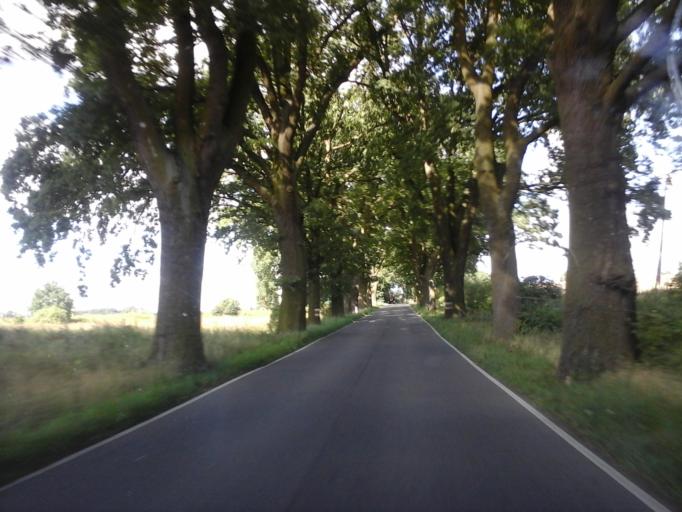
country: PL
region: West Pomeranian Voivodeship
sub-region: Powiat stargardzki
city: Dolice
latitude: 53.1966
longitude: 15.2226
